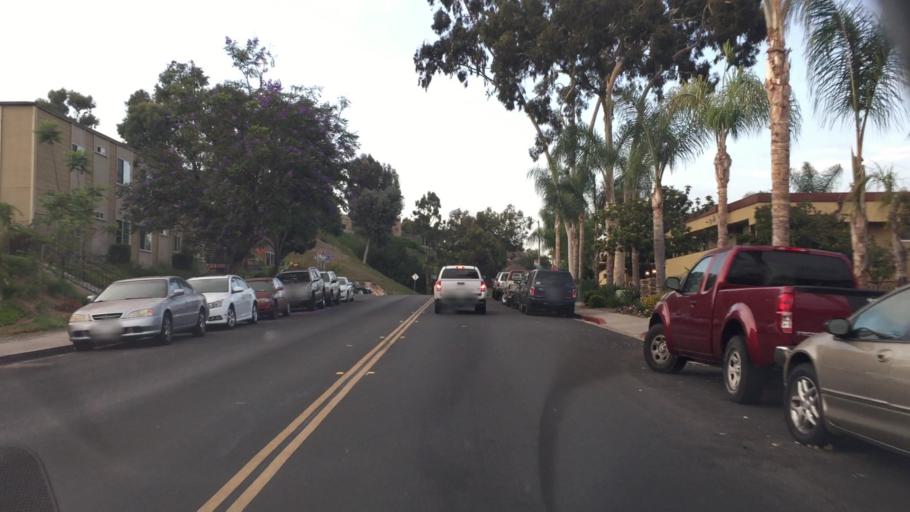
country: US
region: California
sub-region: San Diego County
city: National City
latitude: 32.7234
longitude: -117.0786
